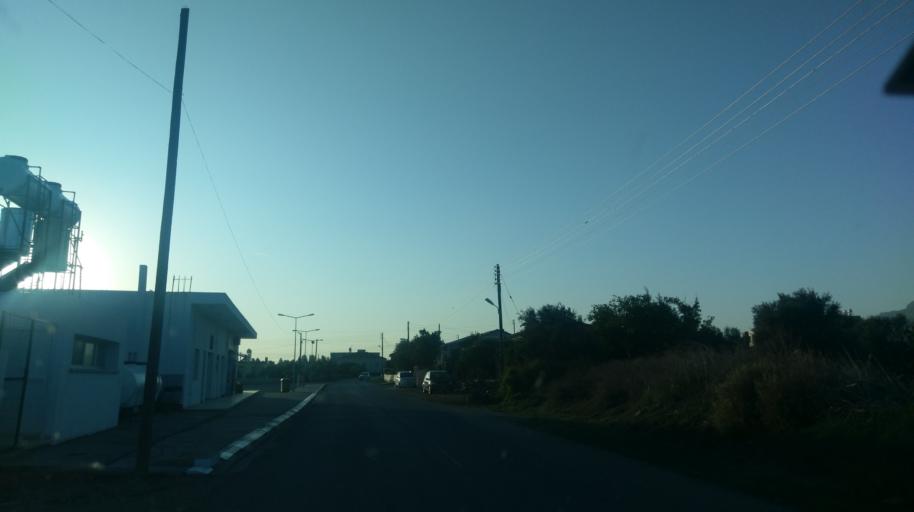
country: CY
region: Lefkosia
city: Nicosia
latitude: 35.2400
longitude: 33.4900
